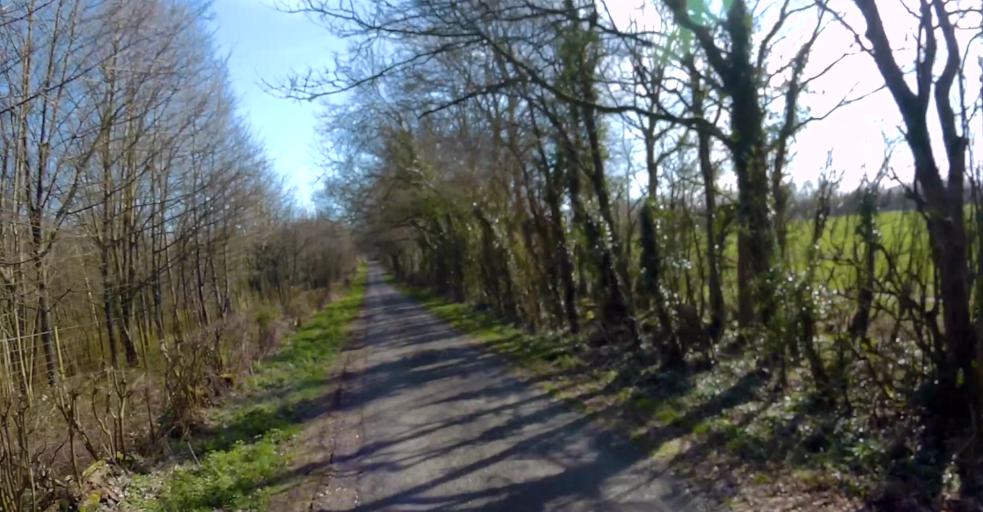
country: GB
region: England
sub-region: Hampshire
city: Four Marks
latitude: 51.1786
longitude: -1.0652
